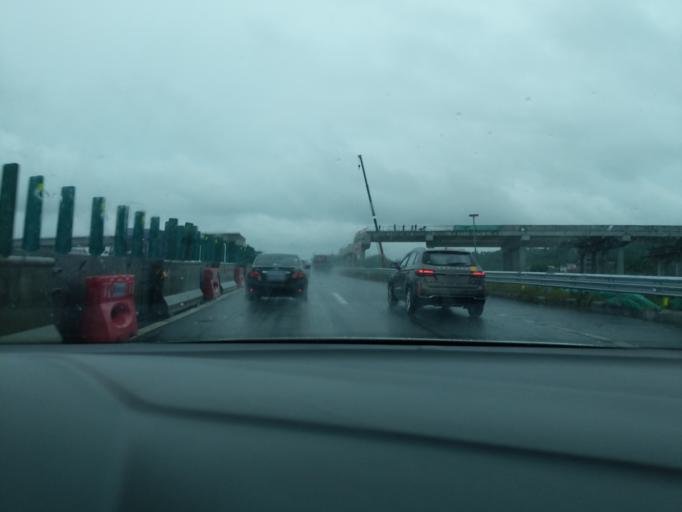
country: CN
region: Guangdong
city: Yueshan
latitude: 22.4633
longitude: 112.7145
